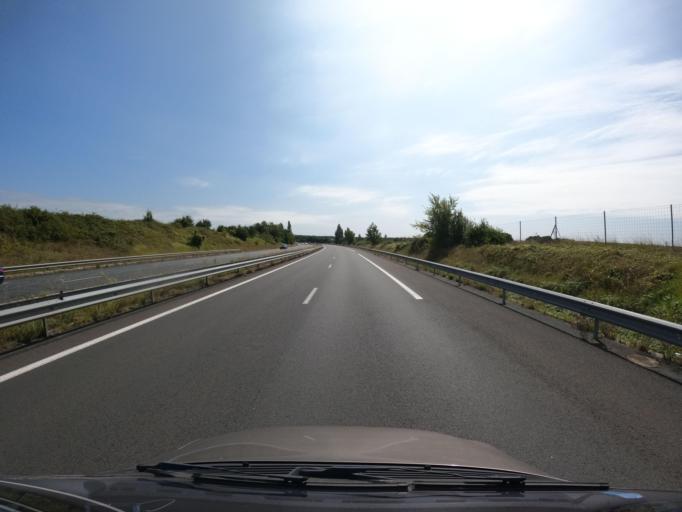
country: FR
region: Poitou-Charentes
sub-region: Departement de la Charente-Maritime
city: Courcon
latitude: 46.2127
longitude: -0.7644
